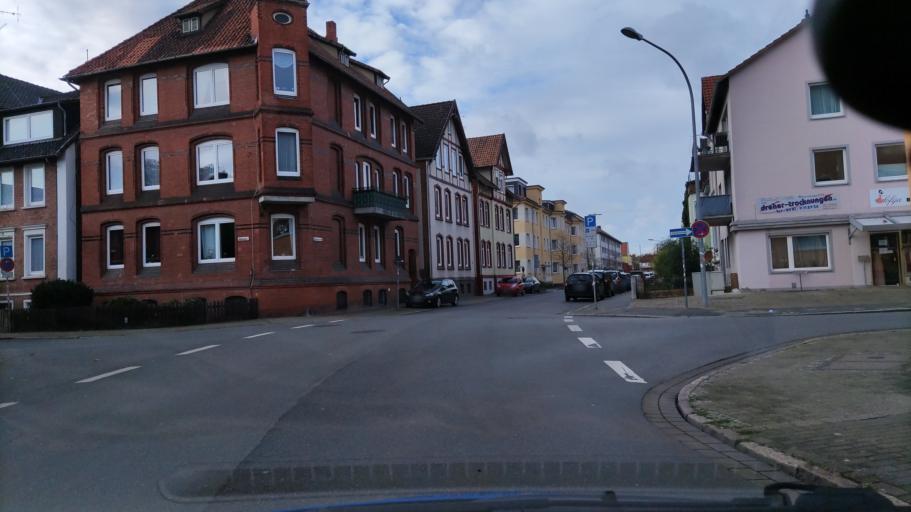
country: DE
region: Lower Saxony
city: Uelzen
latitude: 52.9627
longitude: 10.5538
